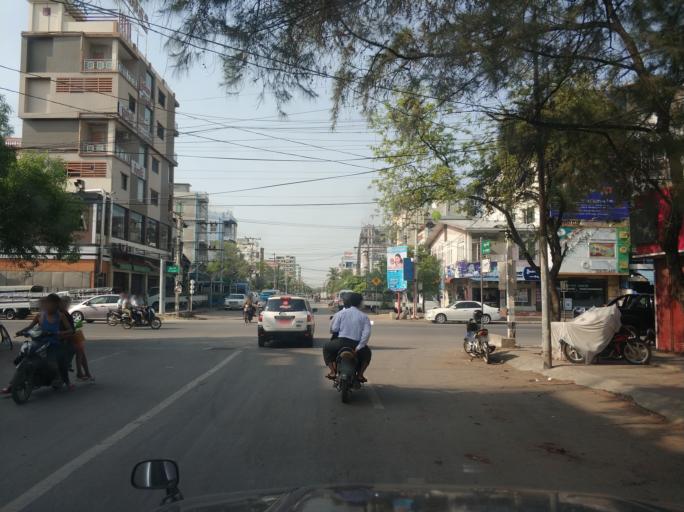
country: MM
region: Mandalay
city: Mandalay
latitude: 21.9691
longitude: 96.0913
